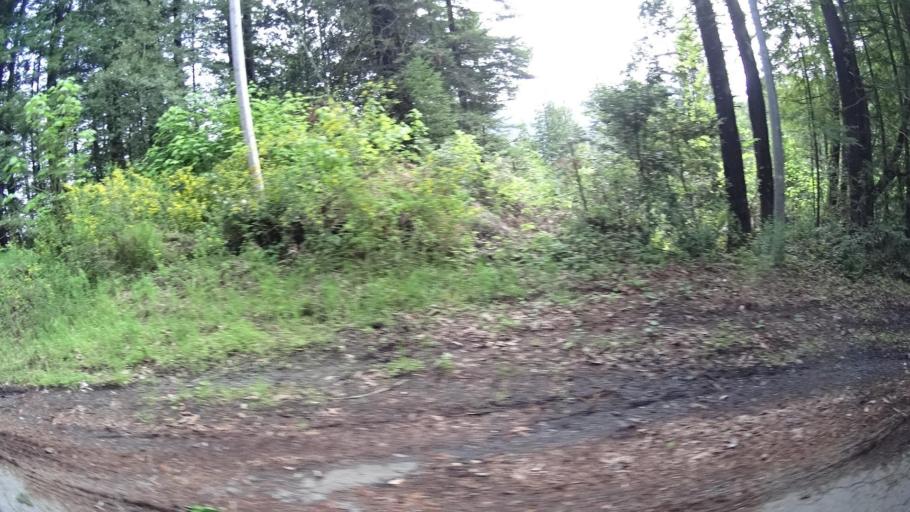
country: US
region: California
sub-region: Humboldt County
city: Redway
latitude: 40.3362
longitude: -123.9057
